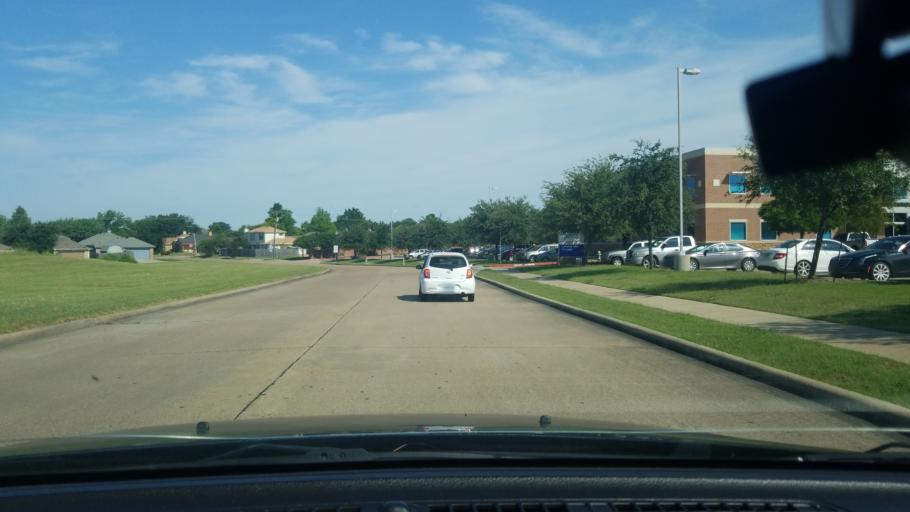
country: US
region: Texas
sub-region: Dallas County
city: Sunnyvale
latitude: 32.7773
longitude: -96.5690
